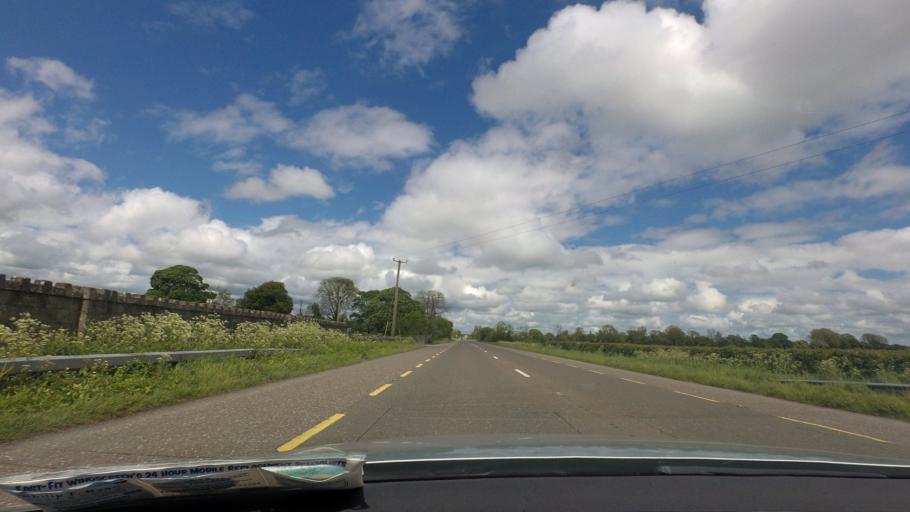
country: IE
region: Munster
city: Thurles
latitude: 52.6052
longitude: -7.7908
